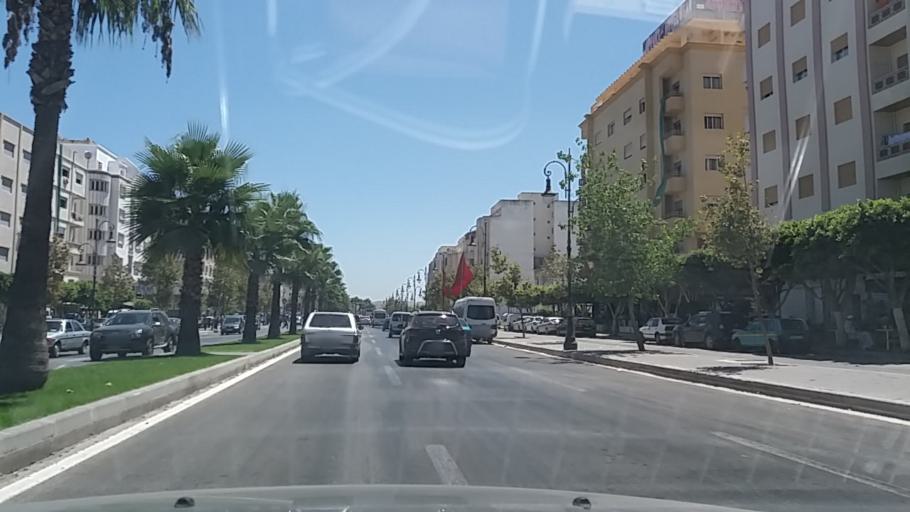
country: MA
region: Tanger-Tetouan
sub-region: Tanger-Assilah
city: Tangier
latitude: 35.7602
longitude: -5.7942
